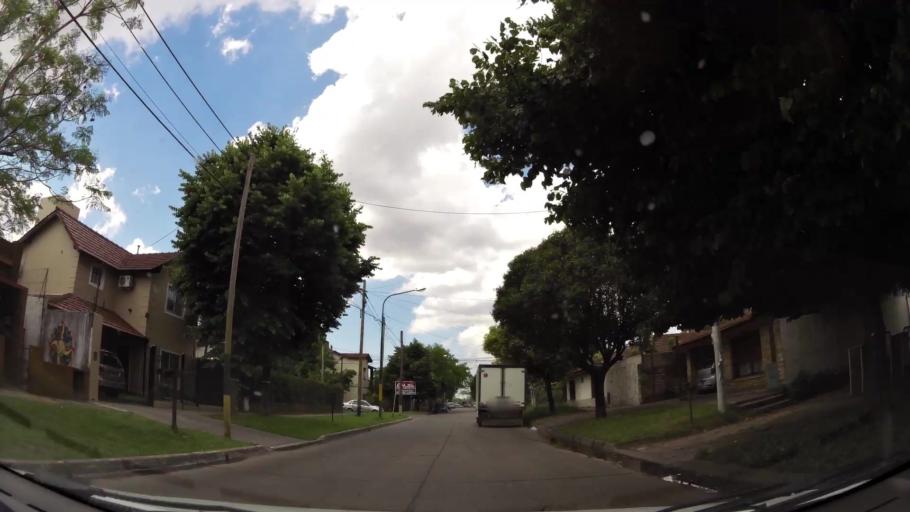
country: AR
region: Buenos Aires
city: Ituzaingo
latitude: -34.6524
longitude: -58.6775
